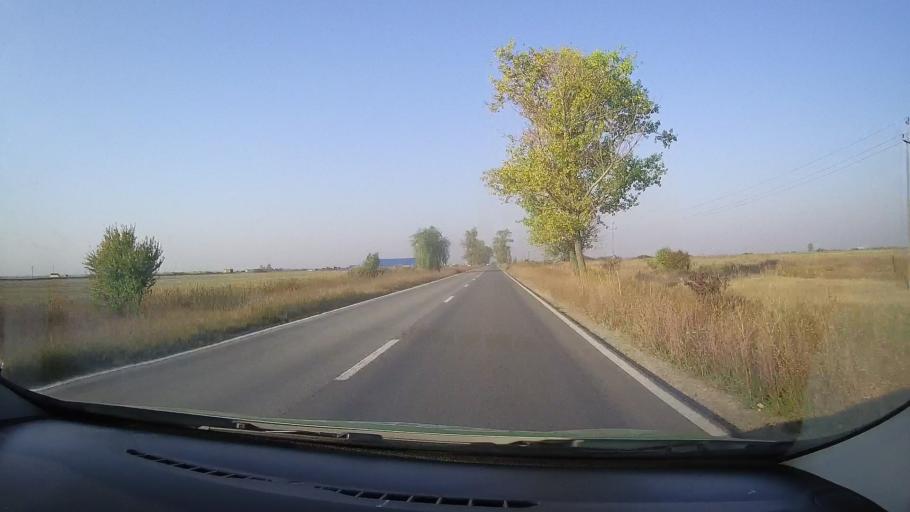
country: RO
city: Chisineu-Cris
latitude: 46.5106
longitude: 21.4805
